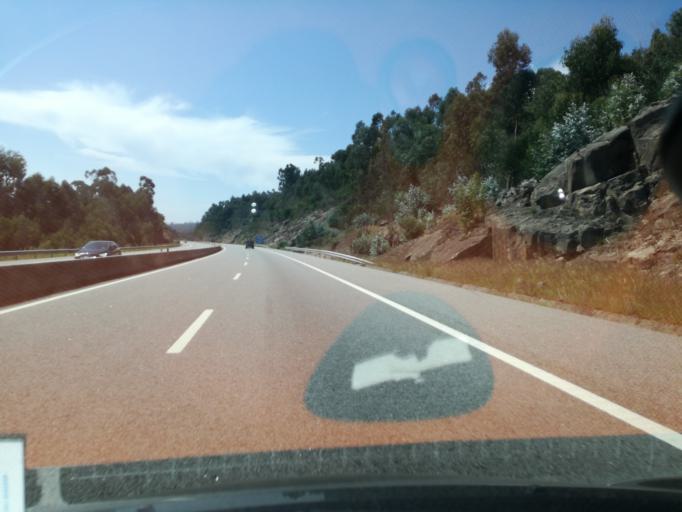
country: PT
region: Viana do Castelo
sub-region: Viana do Castelo
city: Meadela
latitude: 41.7627
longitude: -8.7938
